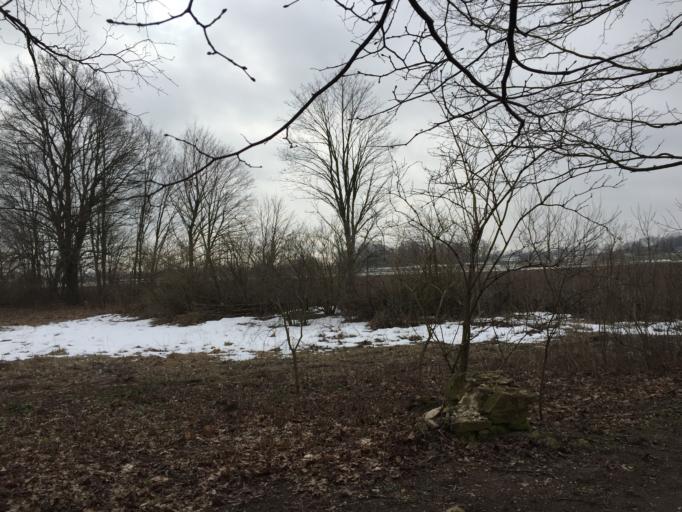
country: LV
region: Rundales
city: Pilsrundale
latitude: 56.5263
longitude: 23.9901
